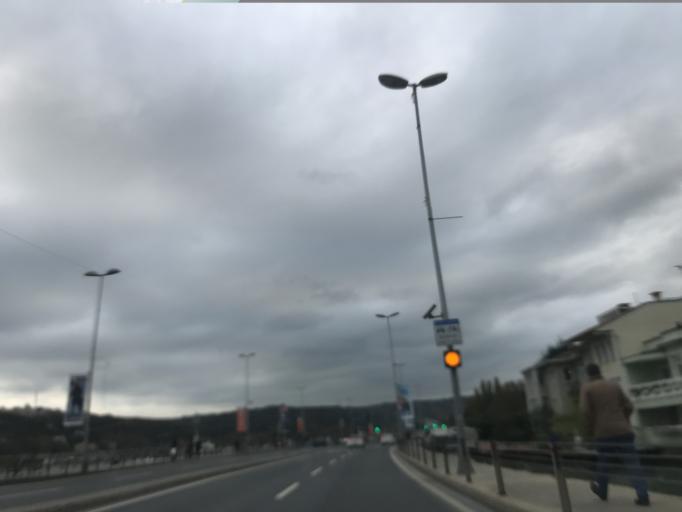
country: TR
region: Istanbul
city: Arikoey
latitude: 41.1599
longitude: 29.0438
